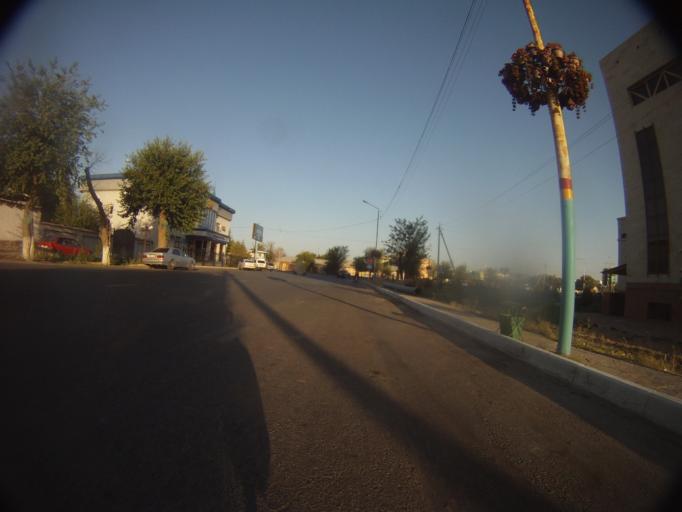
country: KZ
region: Ongtustik Qazaqstan
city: Turkestan
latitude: 43.2995
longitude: 68.2764
